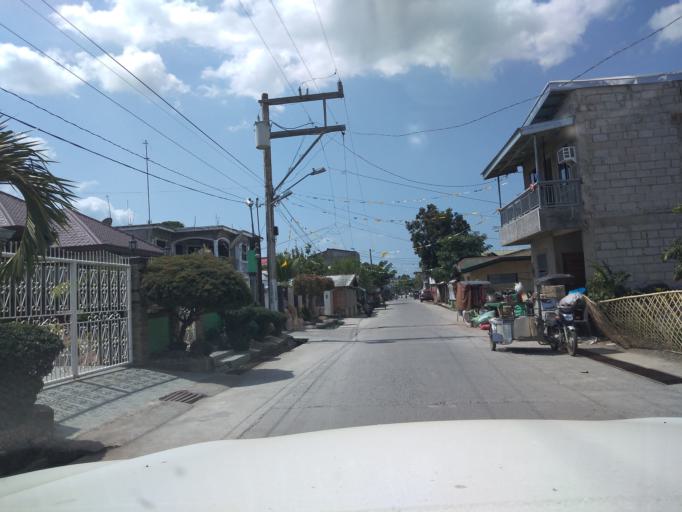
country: PH
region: Central Luzon
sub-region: Province of Pampanga
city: Bahay Pare
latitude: 15.0323
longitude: 120.8802
